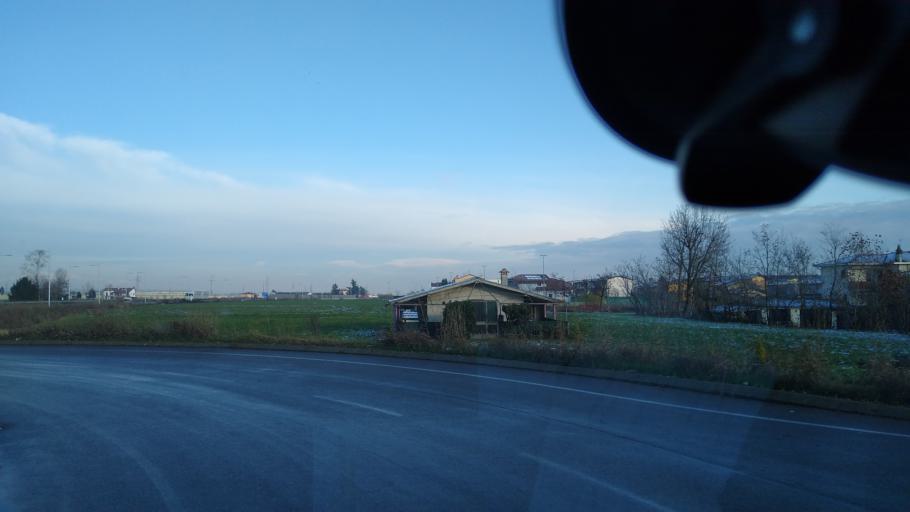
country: IT
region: Lombardy
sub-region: Provincia di Bergamo
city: Caravaggio
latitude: 45.5069
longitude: 9.6348
